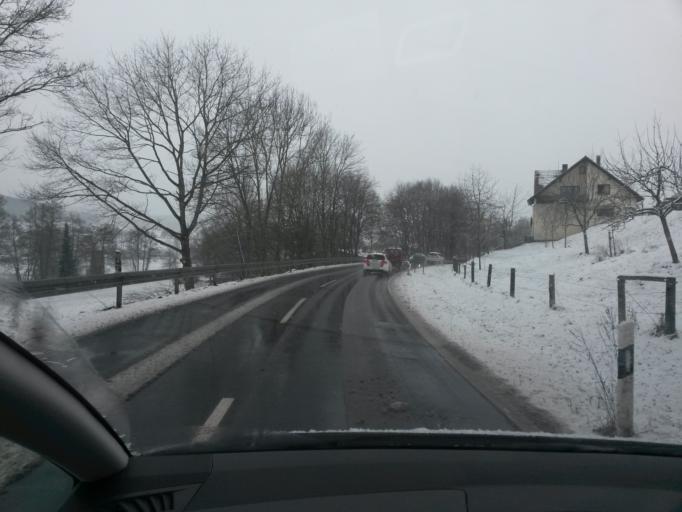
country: DE
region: Hesse
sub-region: Regierungsbezirk Kassel
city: Poppenhausen
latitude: 50.4857
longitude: 9.8199
